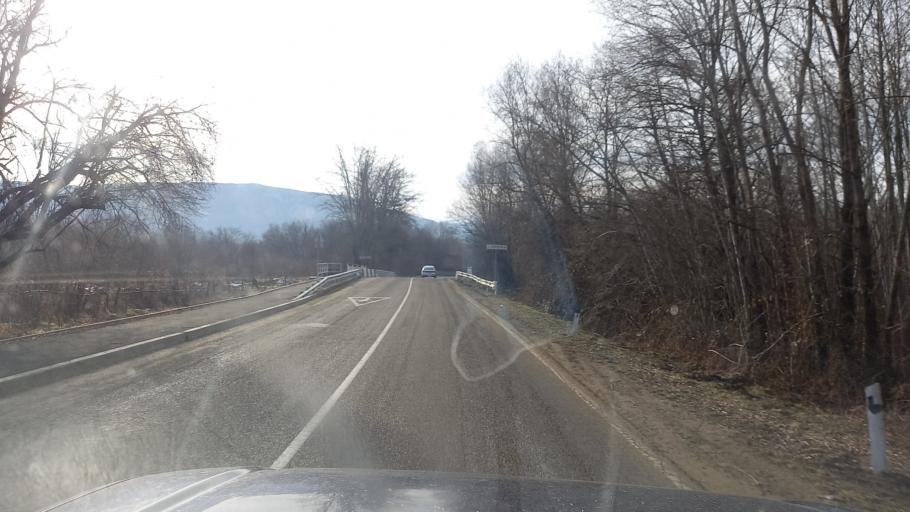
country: RU
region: Krasnodarskiy
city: Neftegorsk
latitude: 44.2743
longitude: 39.9209
